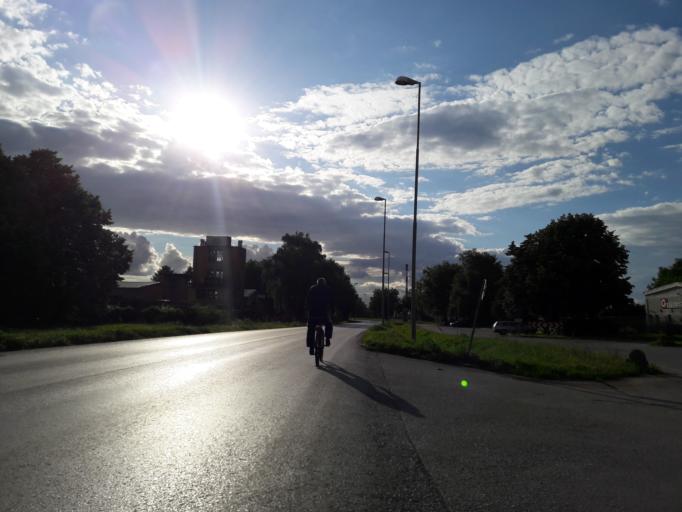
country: HR
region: Osjecko-Baranjska
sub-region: Grad Osijek
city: Osijek
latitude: 45.5452
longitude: 18.7339
